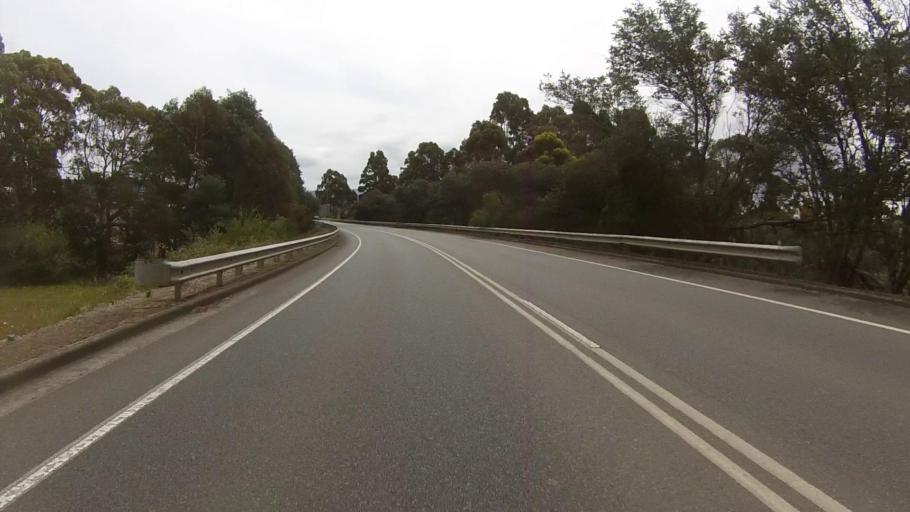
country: AU
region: Tasmania
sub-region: Kingborough
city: Kingston
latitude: -42.9888
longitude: 147.2930
